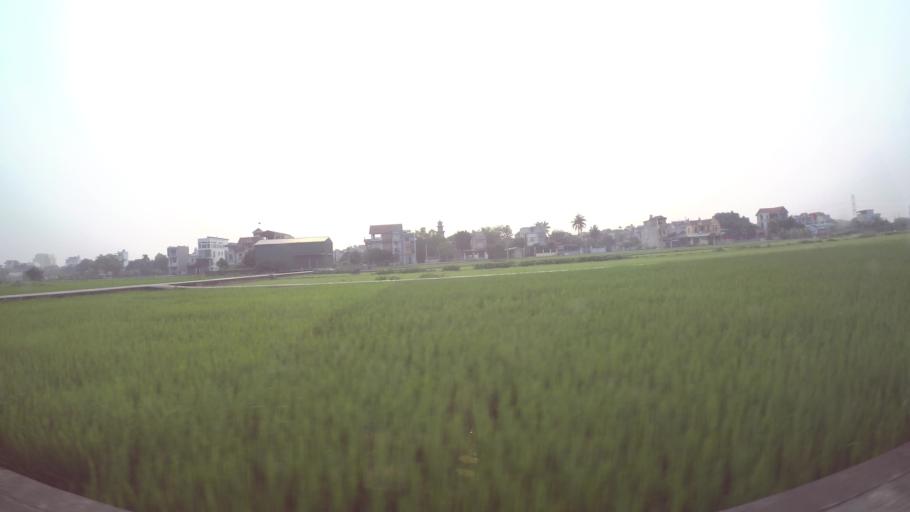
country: VN
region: Ha Noi
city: Thuong Tin
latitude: 20.8757
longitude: 105.8704
